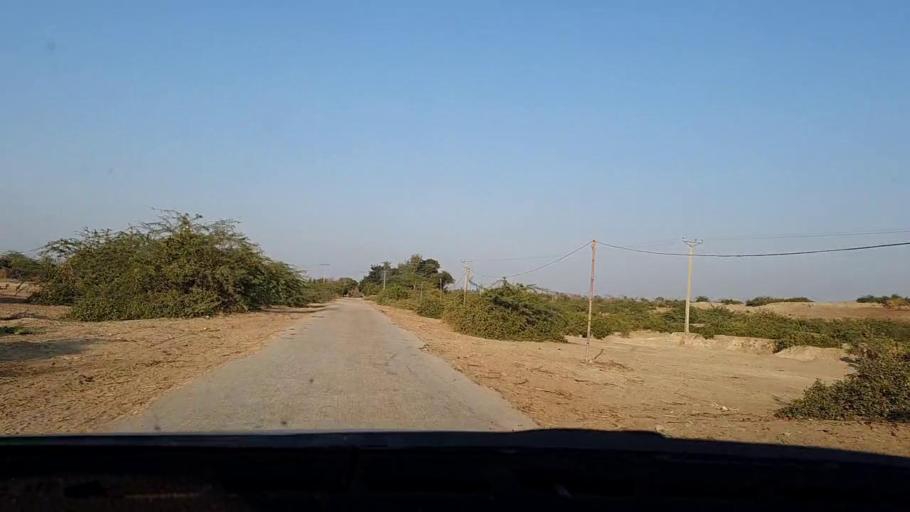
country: PK
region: Sindh
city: Tando Mittha Khan
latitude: 25.8718
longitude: 69.3114
